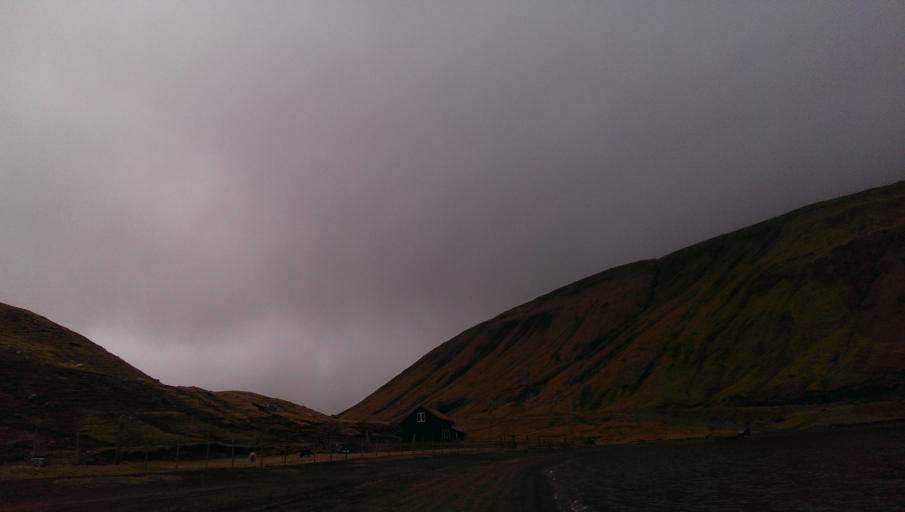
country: FO
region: Streymoy
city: Kollafjordhur
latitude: 62.1304
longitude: -7.0187
